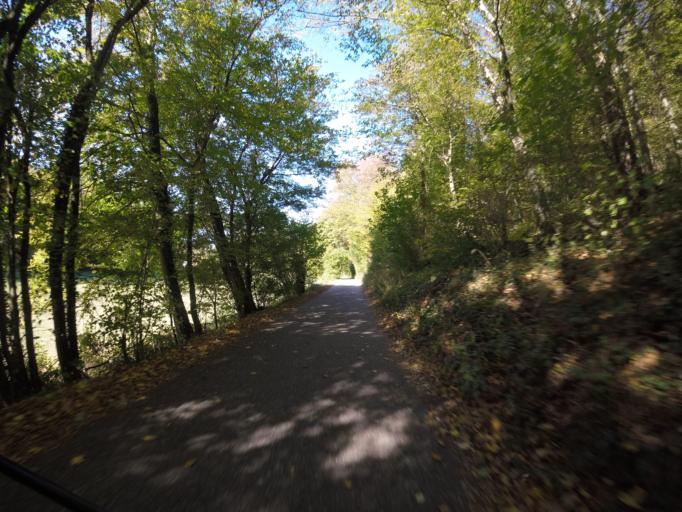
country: DE
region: Baden-Wuerttemberg
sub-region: Karlsruhe Region
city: Knittlingen
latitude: 48.9982
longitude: 8.7376
